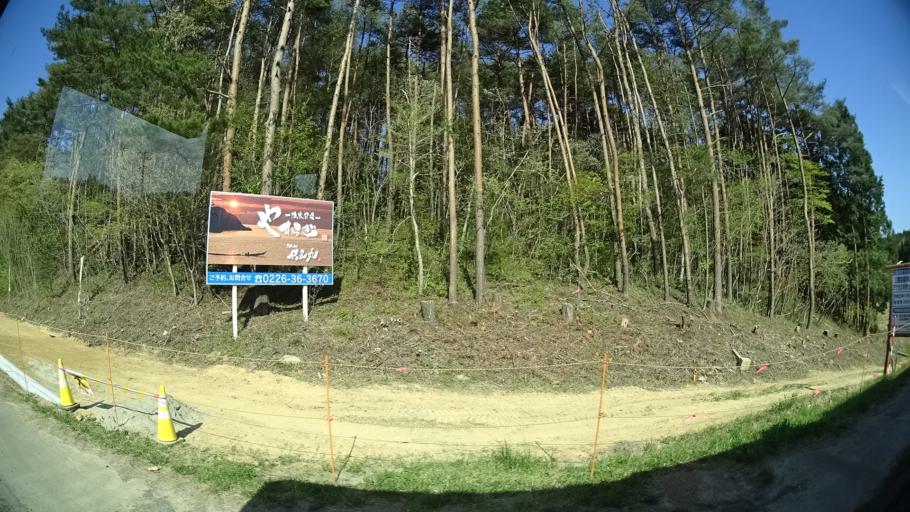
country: JP
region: Miyagi
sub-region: Oshika Gun
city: Onagawa Cho
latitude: 38.7089
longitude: 141.5108
